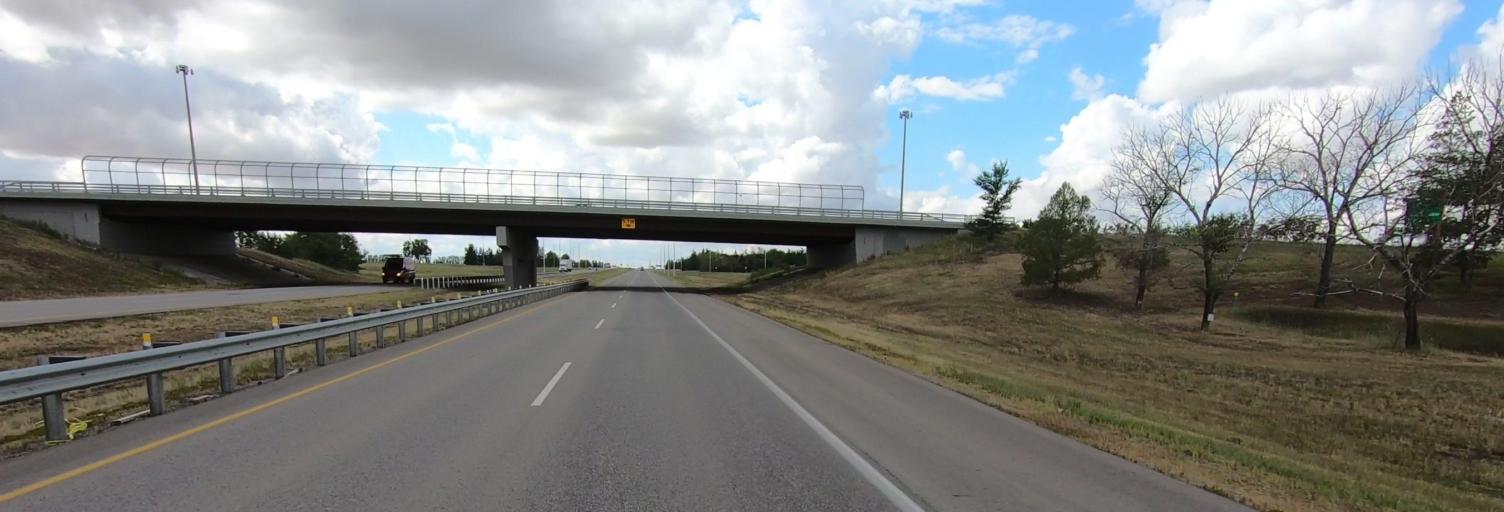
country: CA
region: Saskatchewan
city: Regina
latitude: 50.4087
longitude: -104.5890
